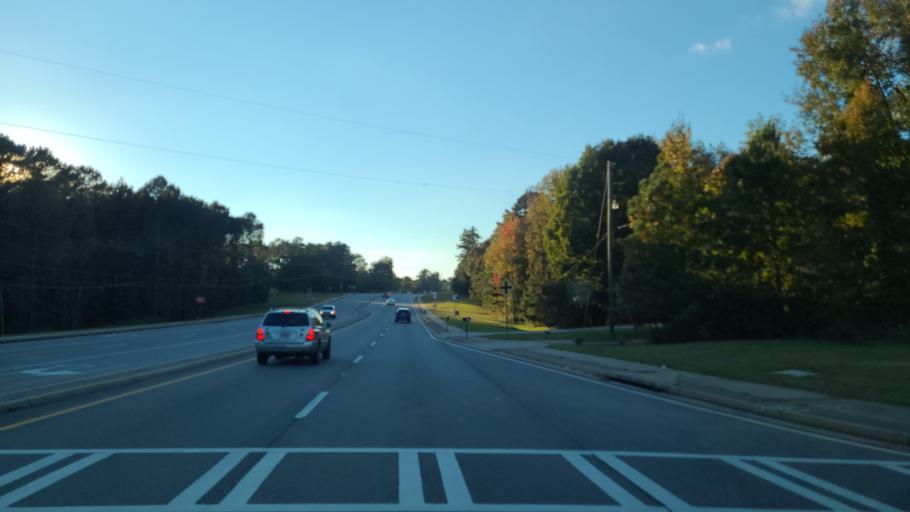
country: US
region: Georgia
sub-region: Clayton County
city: Jonesboro
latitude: 33.5357
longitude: -84.3154
